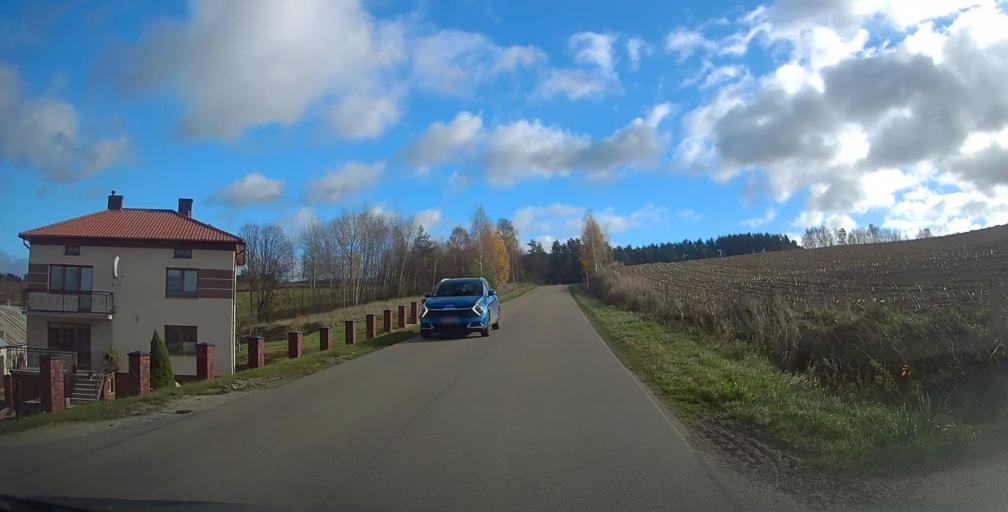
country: PL
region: Podlasie
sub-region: Suwalki
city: Suwalki
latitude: 54.2703
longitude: 22.9219
